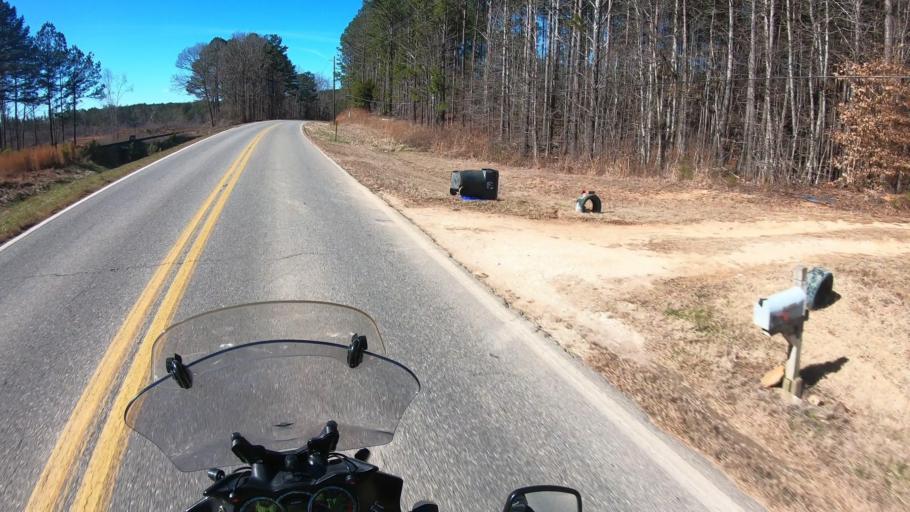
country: US
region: Alabama
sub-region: Cleburne County
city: Heflin
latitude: 33.7276
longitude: -85.4551
